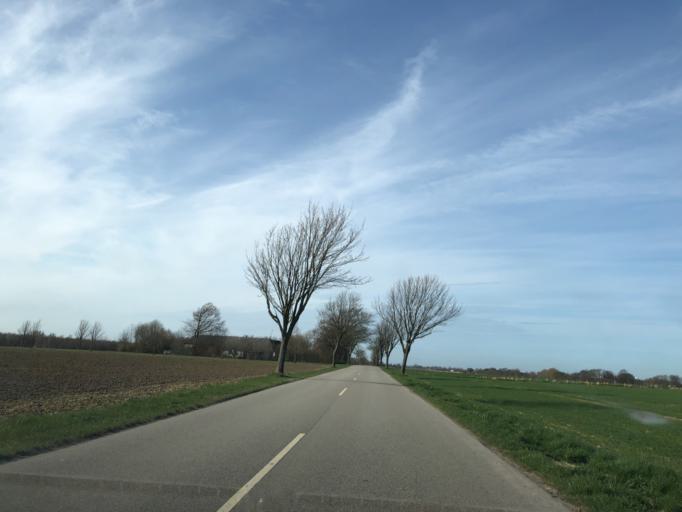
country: DK
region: Zealand
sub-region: Stevns Kommune
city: Store Heddinge
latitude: 55.3048
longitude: 12.4383
